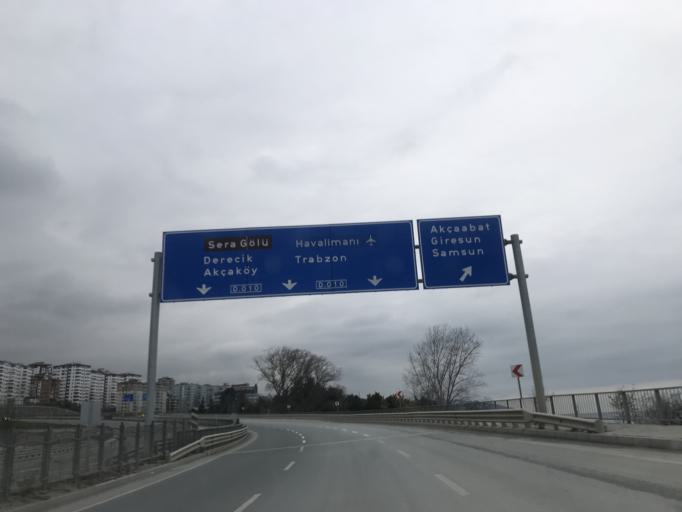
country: TR
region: Trabzon
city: Akcaabat
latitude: 41.0065
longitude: 39.6317
